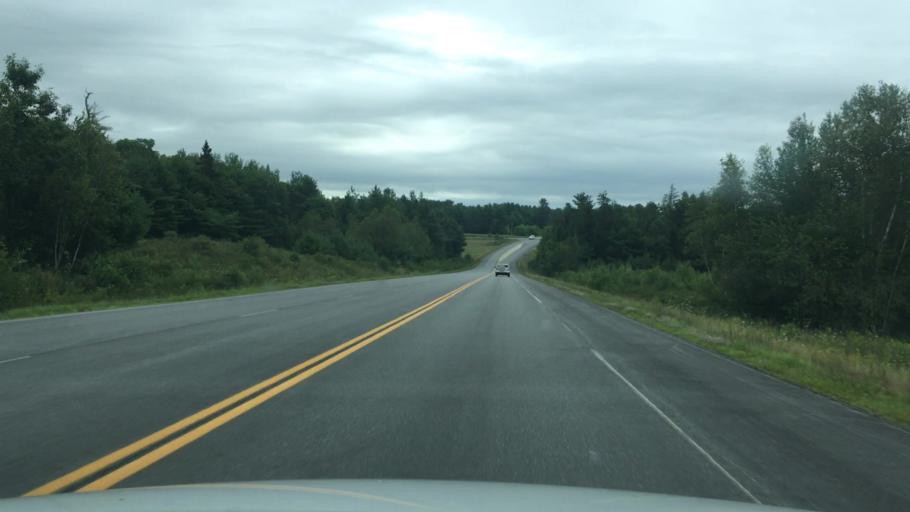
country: US
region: Maine
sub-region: Hancock County
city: Franklin
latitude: 44.8599
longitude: -68.3130
